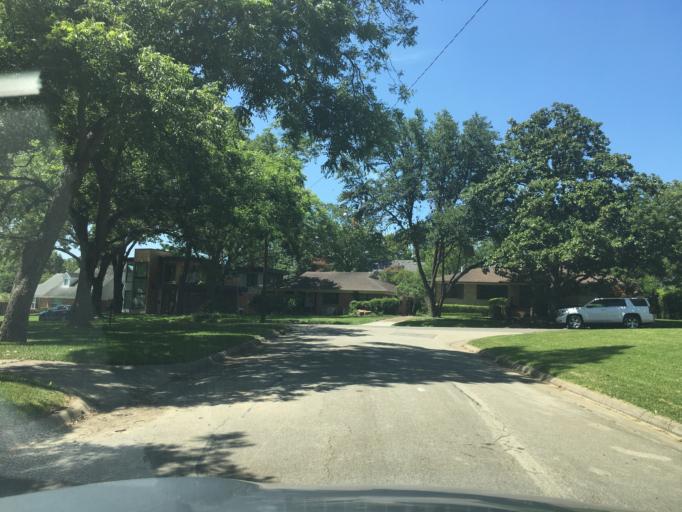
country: US
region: Texas
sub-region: Dallas County
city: Highland Park
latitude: 32.8649
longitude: -96.7299
